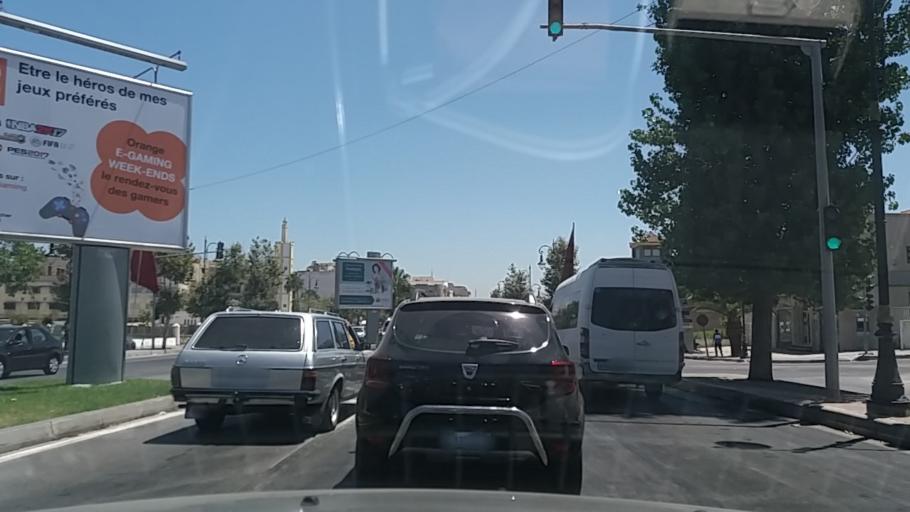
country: MA
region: Tanger-Tetouan
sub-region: Tanger-Assilah
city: Tangier
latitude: 35.7643
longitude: -5.7974
